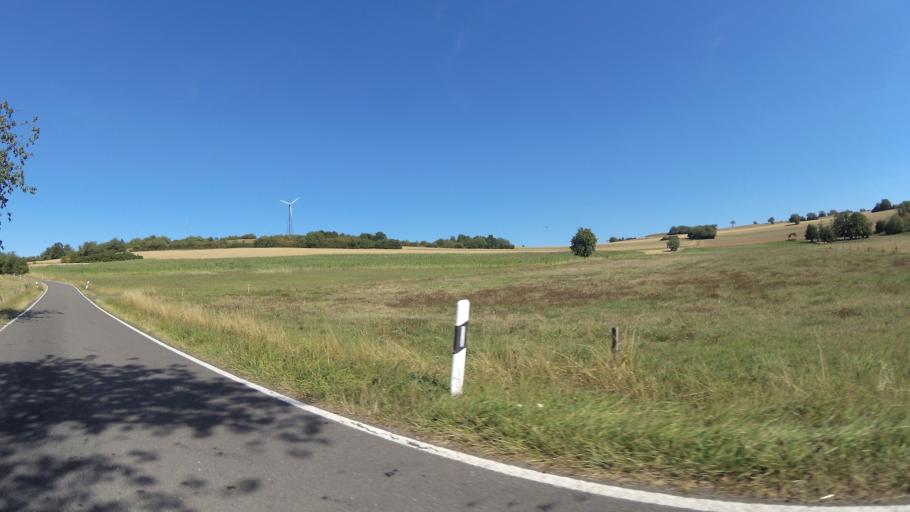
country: FR
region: Lorraine
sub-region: Departement de la Moselle
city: Petit-Rederching
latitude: 49.1333
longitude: 7.3033
